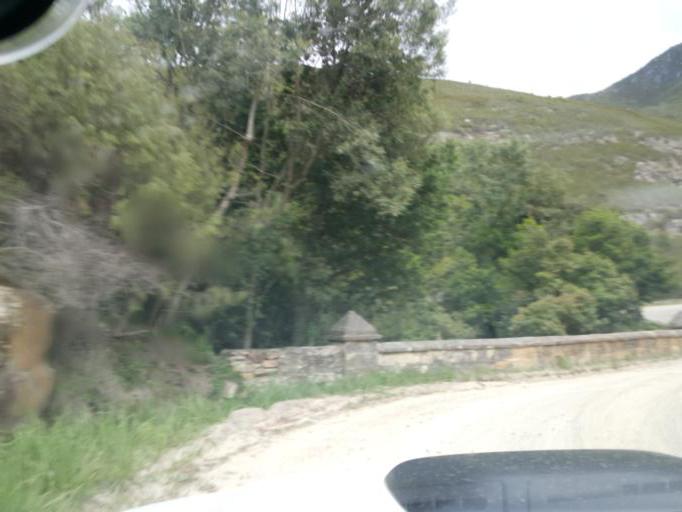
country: ZA
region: Western Cape
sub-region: Eden District Municipality
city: George
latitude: -33.9069
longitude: 22.4188
